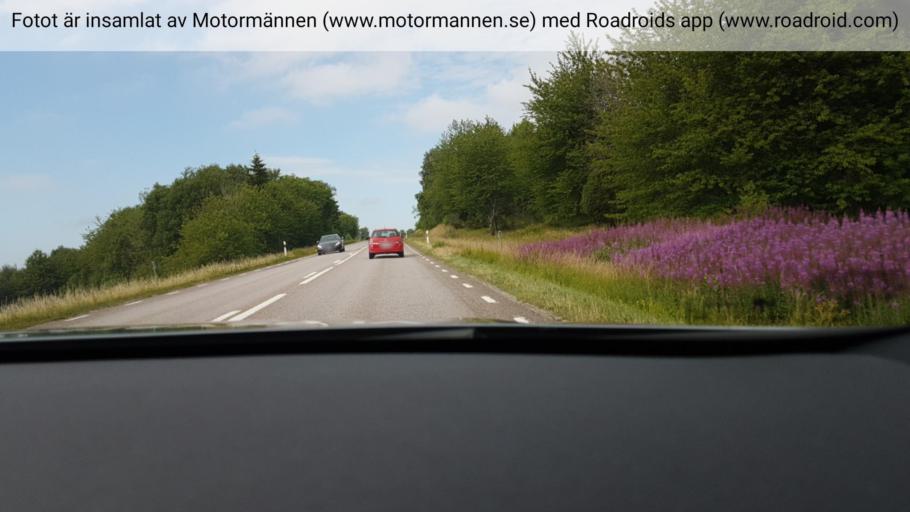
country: SE
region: Vaestra Goetaland
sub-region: Skovde Kommun
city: Skultorp
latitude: 58.2931
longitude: 13.7856
